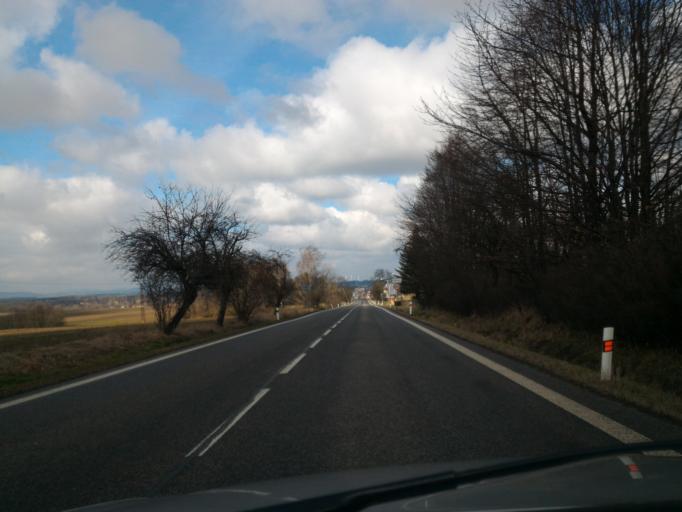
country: PL
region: Silesian Voivodeship
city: Zawidow
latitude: 51.0104
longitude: 15.0686
